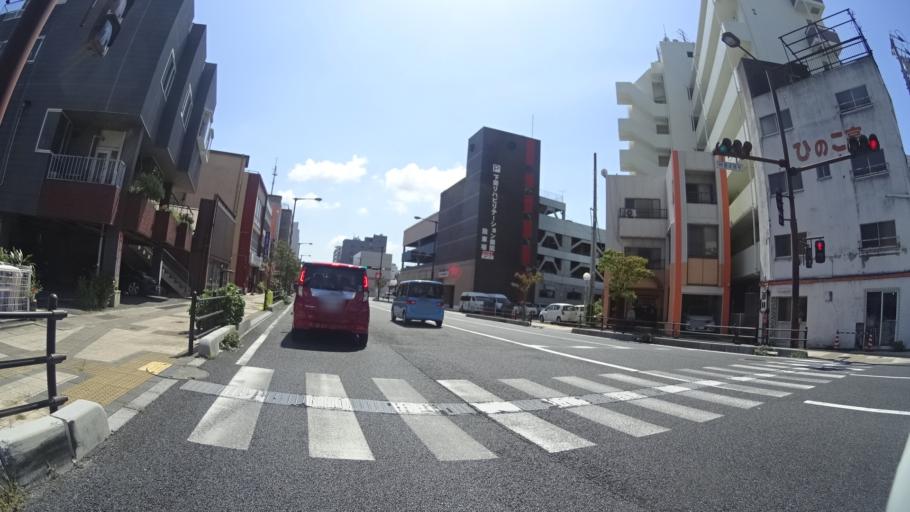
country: JP
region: Yamaguchi
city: Shimonoseki
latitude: 33.9538
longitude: 130.9202
